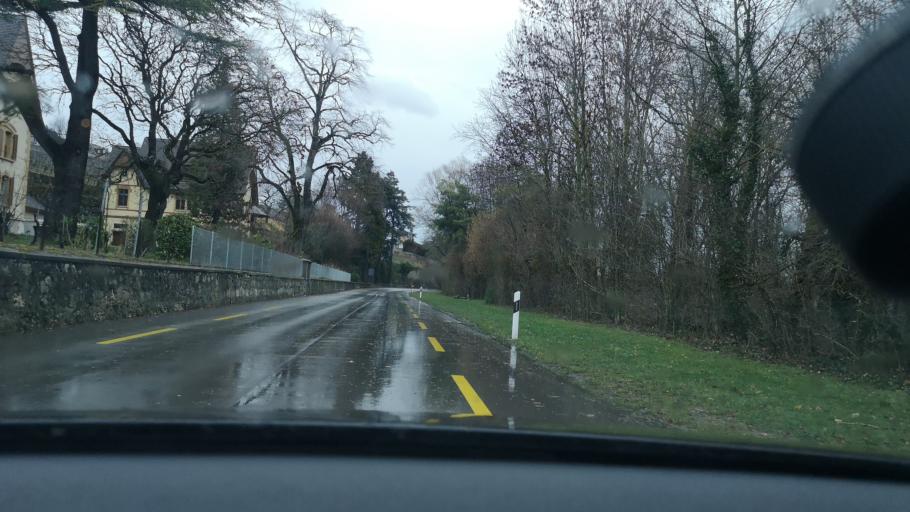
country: CH
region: Neuchatel
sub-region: Boudry District
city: Auvernier
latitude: 46.9769
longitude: 6.8814
